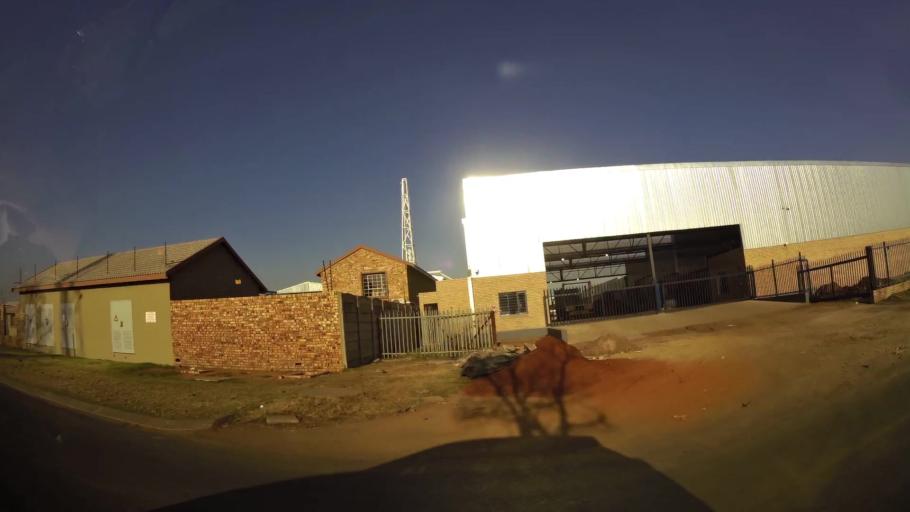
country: ZA
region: Gauteng
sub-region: West Rand District Municipality
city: Randfontein
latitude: -26.1955
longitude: 27.6848
